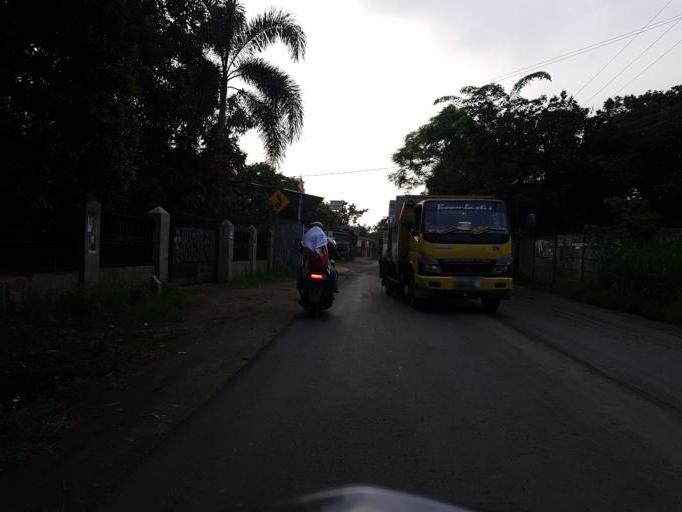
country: ID
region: West Java
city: Parung
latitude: -6.4727
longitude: 106.7191
